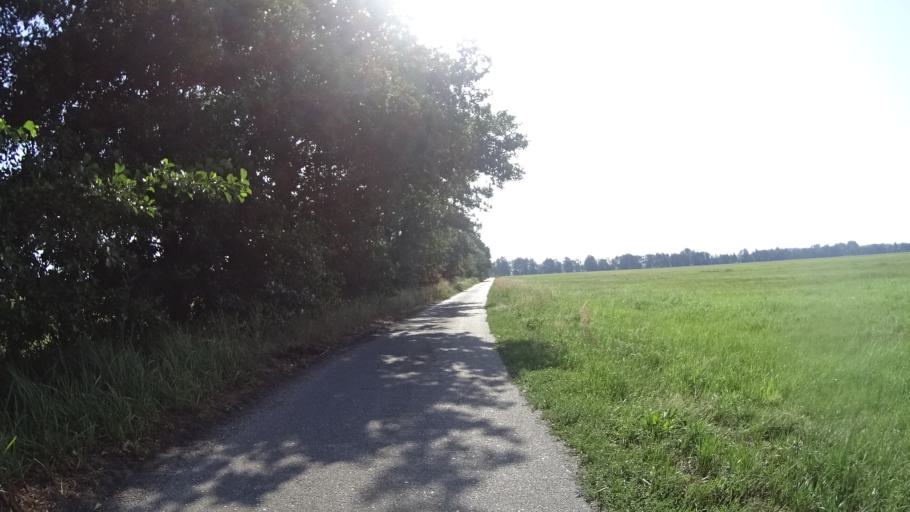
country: DE
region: Brandenburg
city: Neu Zauche
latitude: 51.9081
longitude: 14.0638
